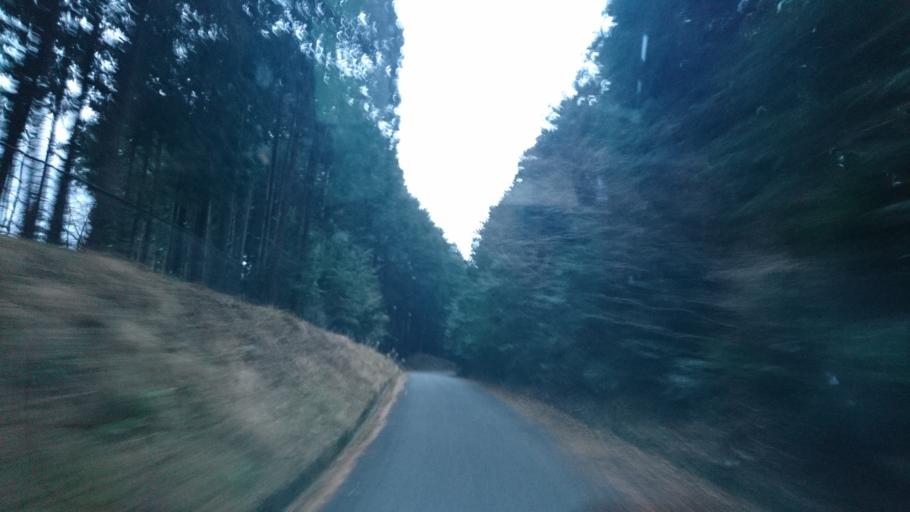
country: JP
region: Shizuoka
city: Fujinomiya
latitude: 35.3306
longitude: 138.5787
